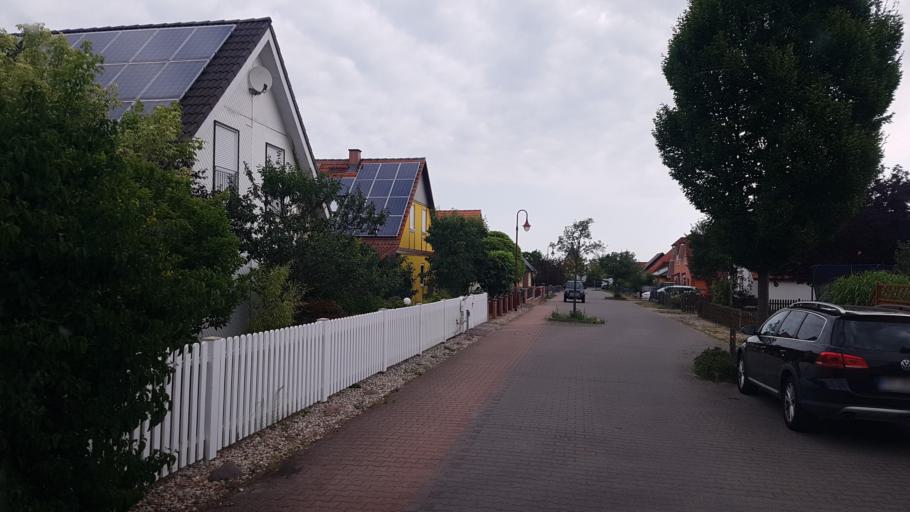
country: DE
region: Brandenburg
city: Linthe
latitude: 52.1511
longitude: 12.7836
